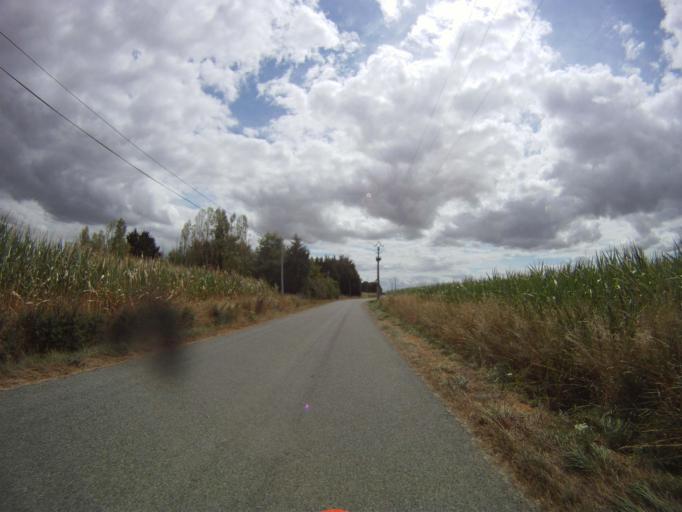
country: FR
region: Centre
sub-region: Departement du Loir-et-Cher
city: Montoire-sur-le-Loir
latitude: 47.6982
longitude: 0.8009
